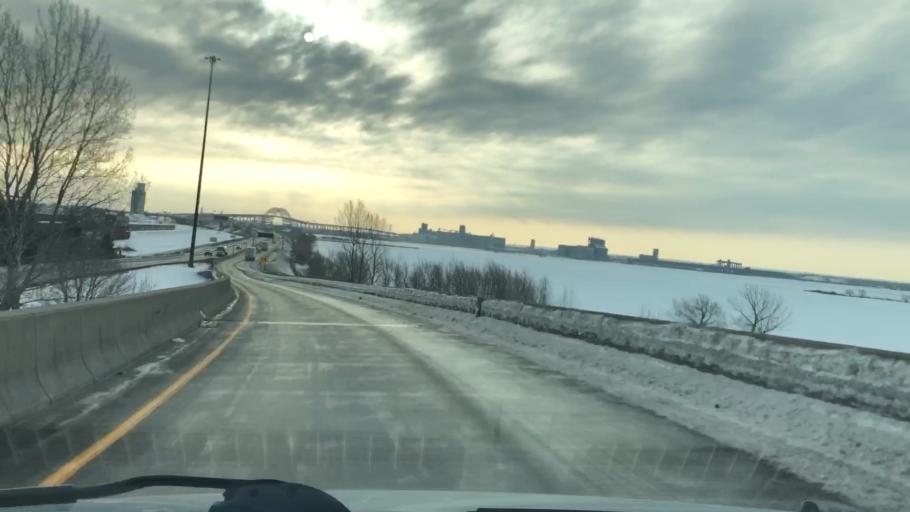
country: US
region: Minnesota
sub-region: Saint Louis County
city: Duluth
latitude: 46.7657
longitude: -92.1205
